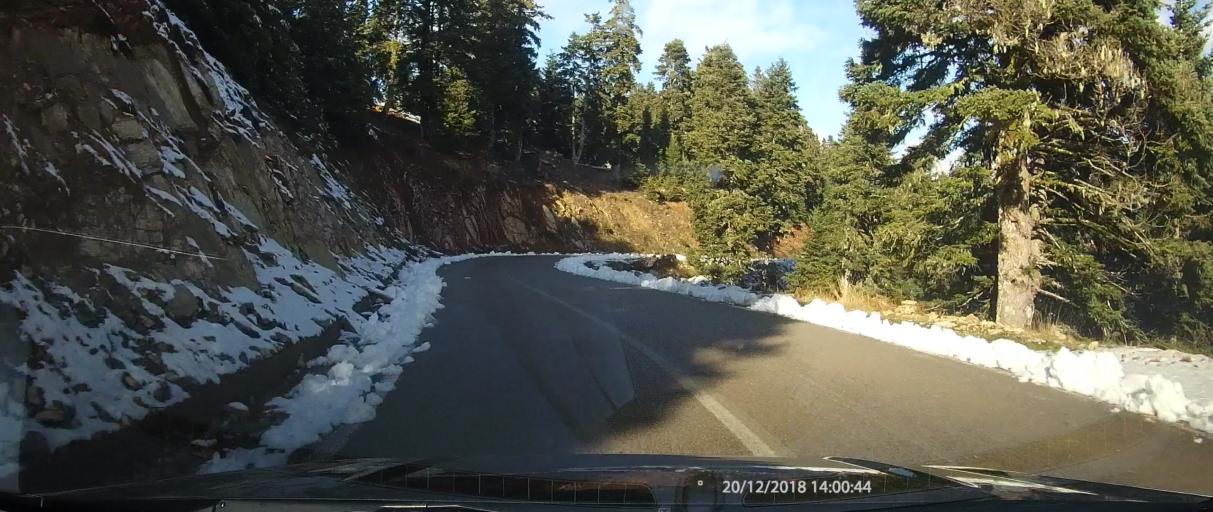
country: GR
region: West Greece
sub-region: Nomos Aitolias kai Akarnanias
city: Thermo
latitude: 38.7268
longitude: 21.6277
